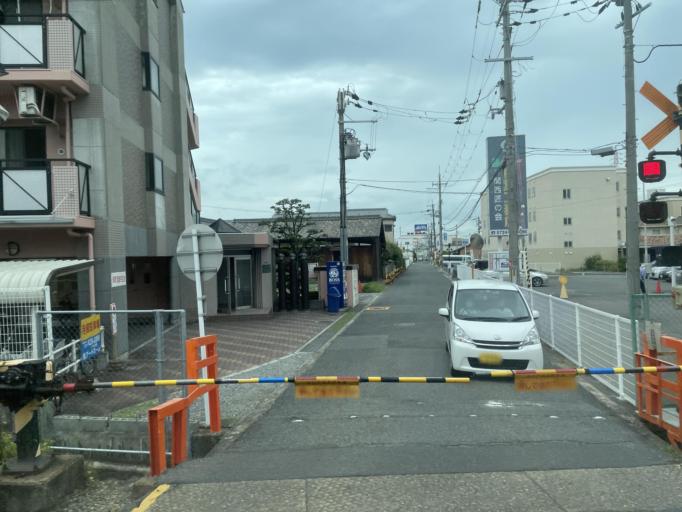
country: JP
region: Osaka
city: Kishiwada
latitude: 34.4570
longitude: 135.3963
